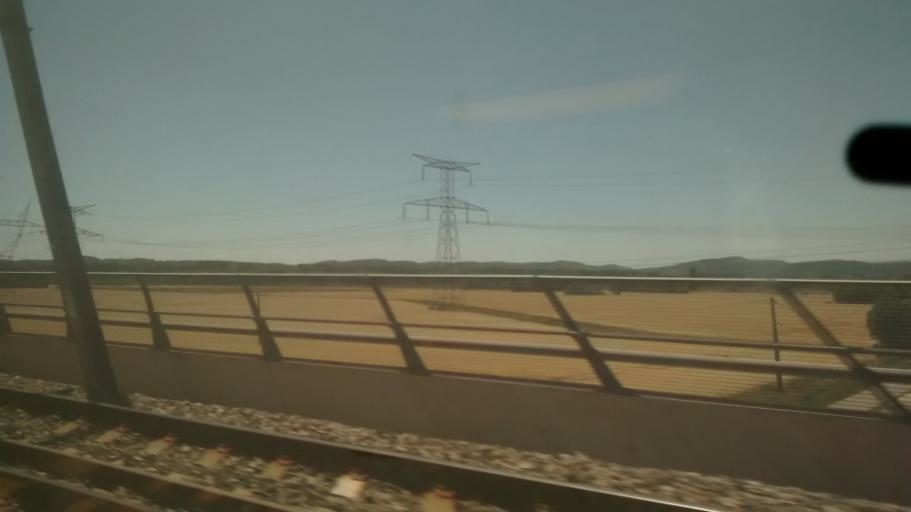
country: FR
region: Provence-Alpes-Cote d'Azur
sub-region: Departement du Vaucluse
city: Mondragon
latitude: 44.2475
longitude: 4.6915
